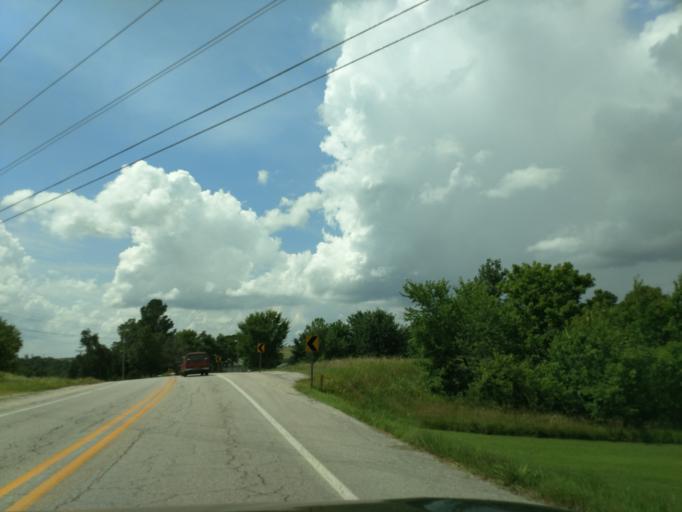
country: US
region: Arkansas
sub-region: Boone County
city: Harrison
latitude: 36.2885
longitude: -93.2363
